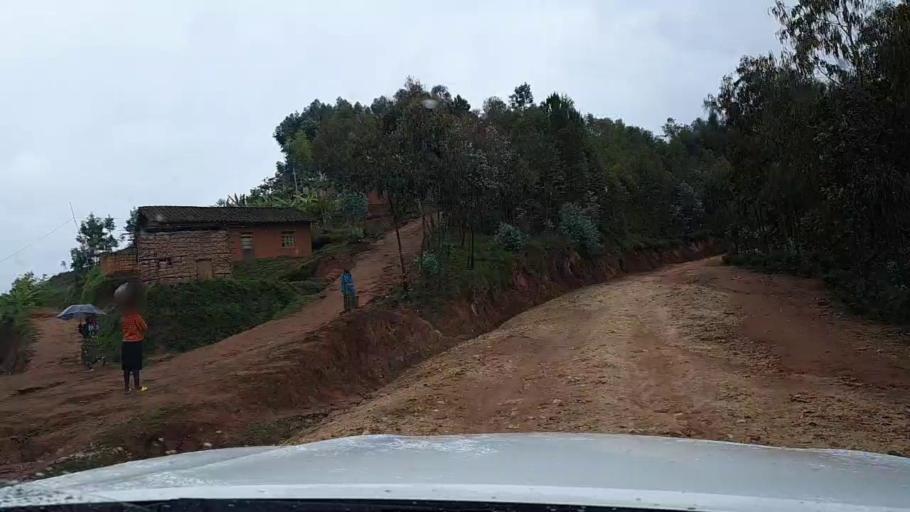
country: RW
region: Southern Province
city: Nzega
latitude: -2.4601
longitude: 29.4928
